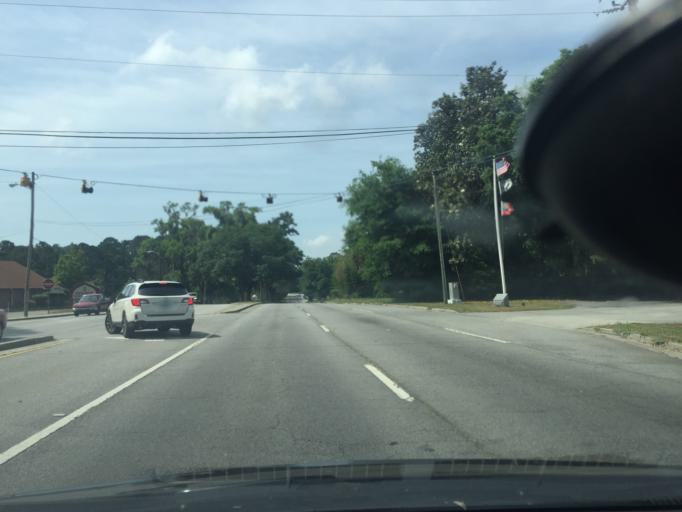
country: US
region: Georgia
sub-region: Chatham County
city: Montgomery
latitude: 31.9867
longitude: -81.1293
